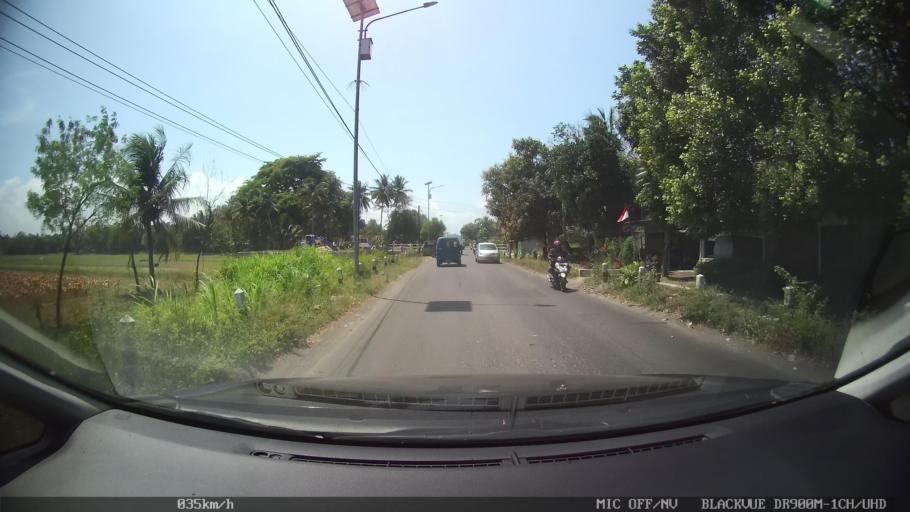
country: ID
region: Daerah Istimewa Yogyakarta
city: Srandakan
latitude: -7.9512
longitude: 110.2112
